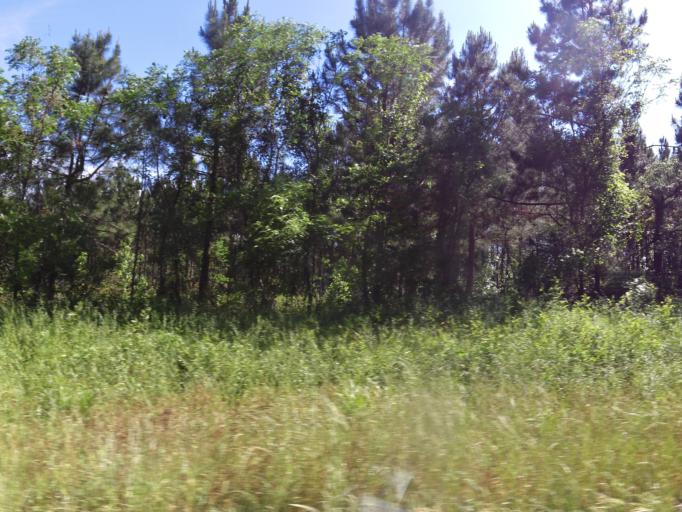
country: US
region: South Carolina
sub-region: Barnwell County
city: Blackville
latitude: 33.3468
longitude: -81.2067
